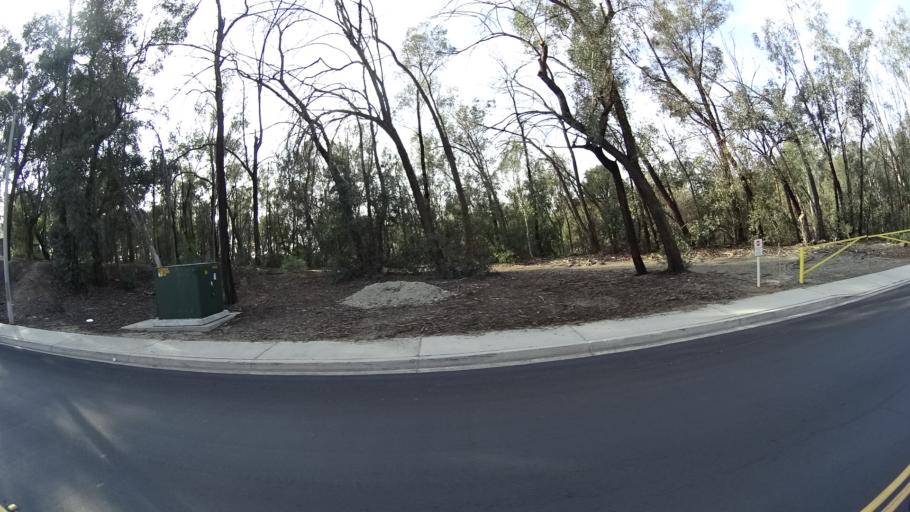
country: US
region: California
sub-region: Orange County
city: Lake Forest
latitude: 33.6500
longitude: -117.6820
